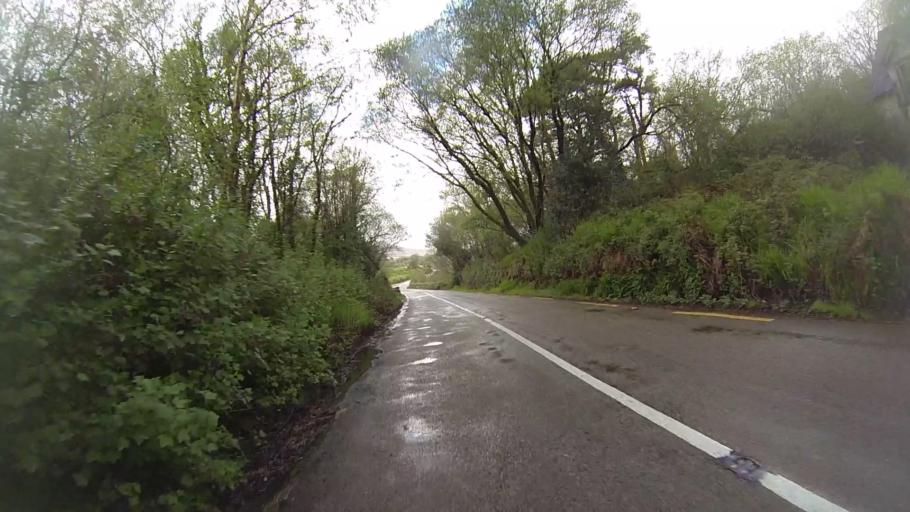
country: IE
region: Munster
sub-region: Ciarrai
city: Kenmare
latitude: 51.8892
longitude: -9.7685
